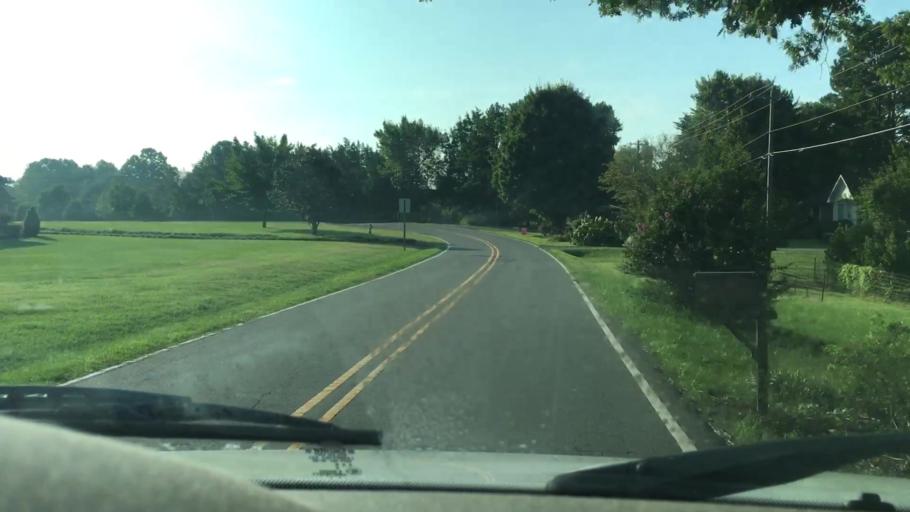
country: US
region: North Carolina
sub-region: Mecklenburg County
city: Huntersville
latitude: 35.4362
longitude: -80.8136
